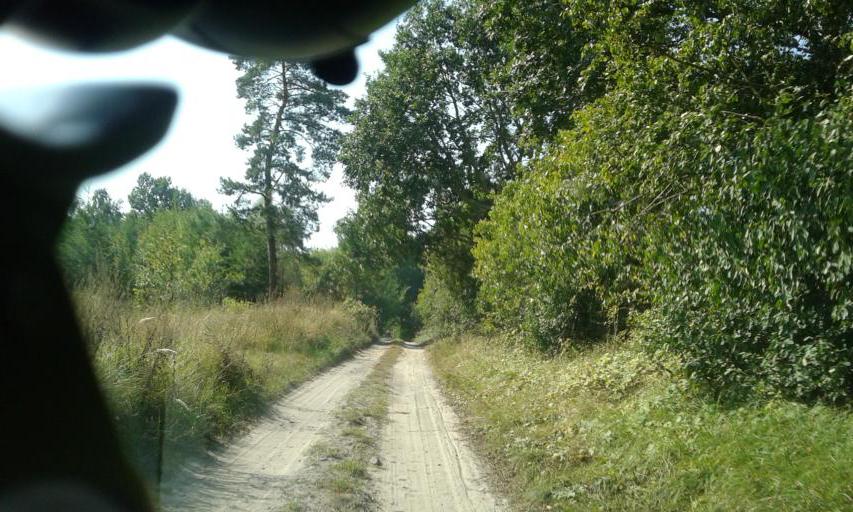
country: PL
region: West Pomeranian Voivodeship
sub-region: Powiat choszczenski
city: Krzecin
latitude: 53.0707
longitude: 15.5541
